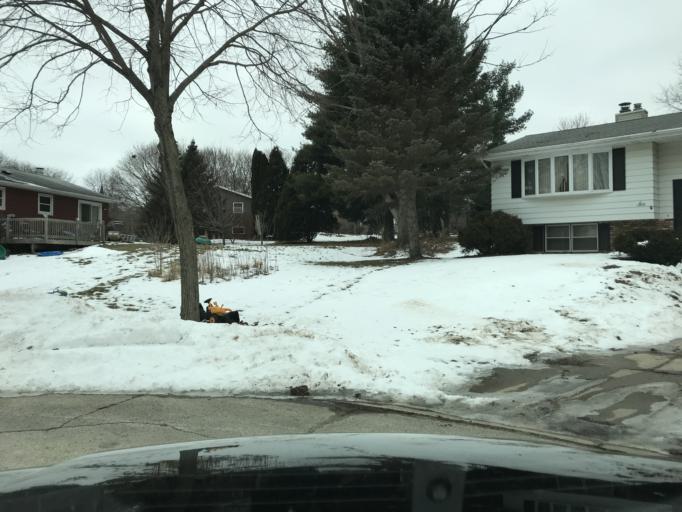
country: US
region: Wisconsin
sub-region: Dane County
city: Monona
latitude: 43.0800
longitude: -89.2849
